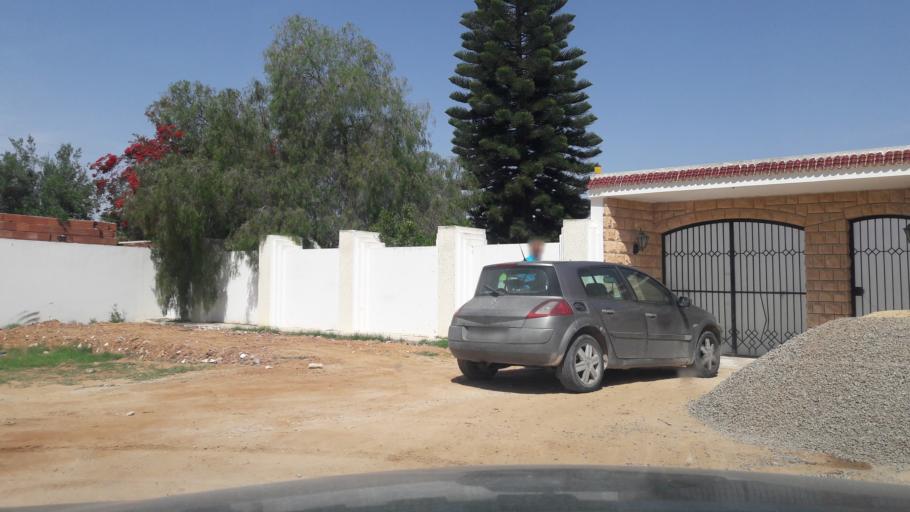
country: TN
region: Safaqis
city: Sfax
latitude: 34.7894
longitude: 10.7537
